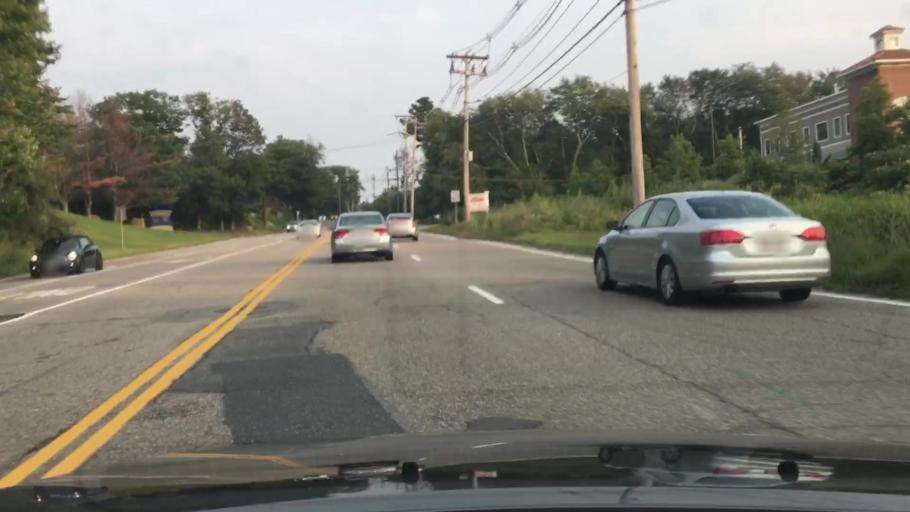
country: US
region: Massachusetts
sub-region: Middlesex County
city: Hopkinton
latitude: 42.2110
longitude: -71.5504
